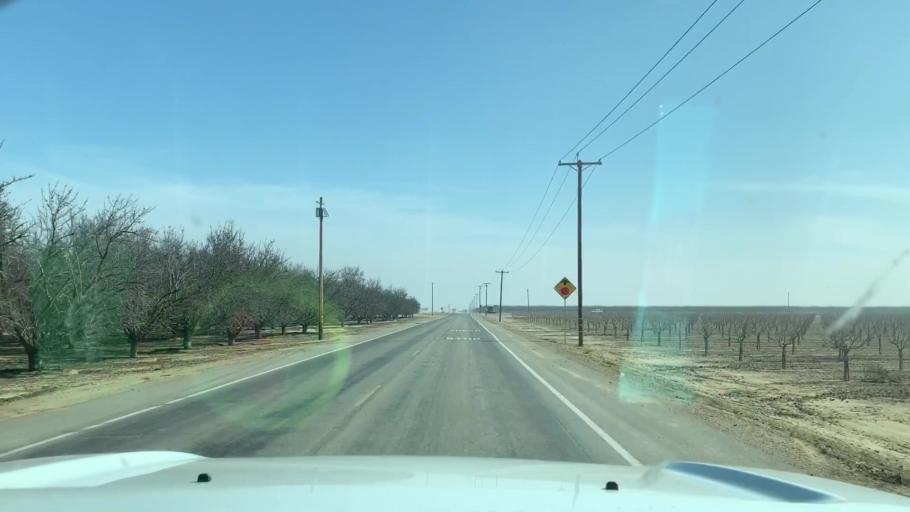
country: US
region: California
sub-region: Kern County
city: Buttonwillow
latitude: 35.4424
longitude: -119.4774
